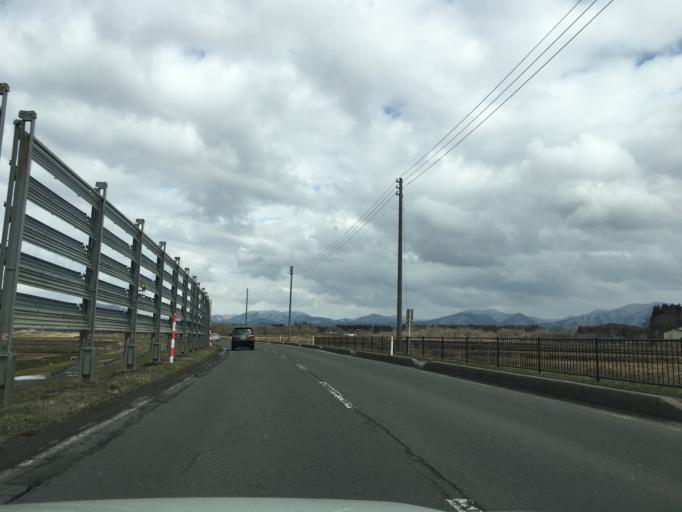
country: JP
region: Akita
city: Hanawa
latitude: 40.2487
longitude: 140.7557
